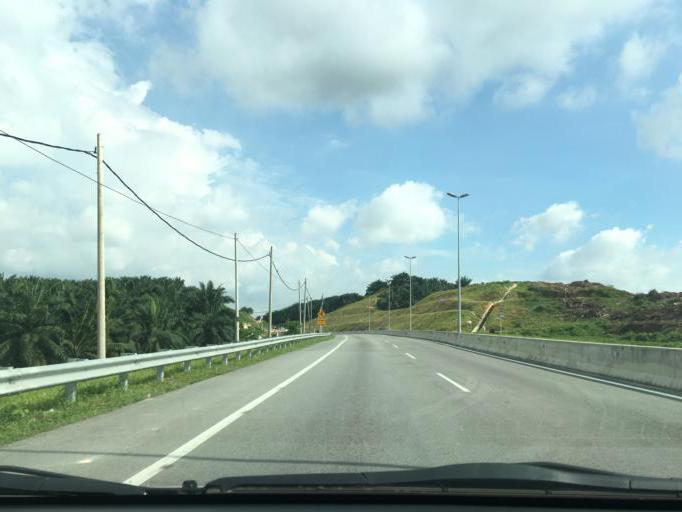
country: MY
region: Selangor
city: Batu Arang
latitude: 3.2917
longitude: 101.4412
